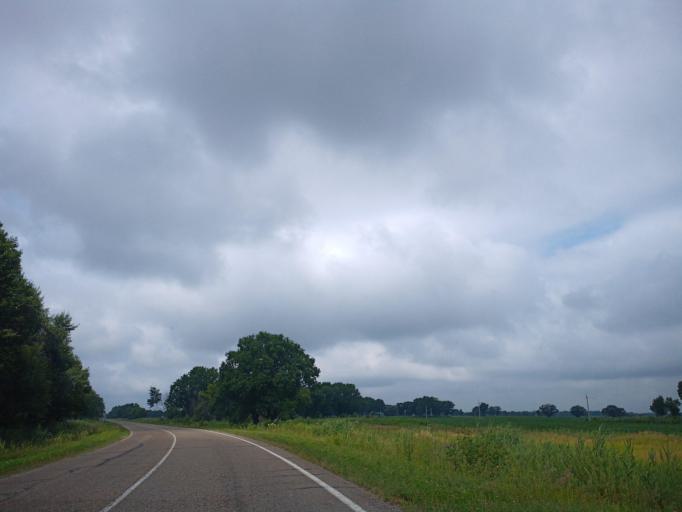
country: RU
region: Primorskiy
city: Dal'nerechensk
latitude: 45.9486
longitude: 133.9092
